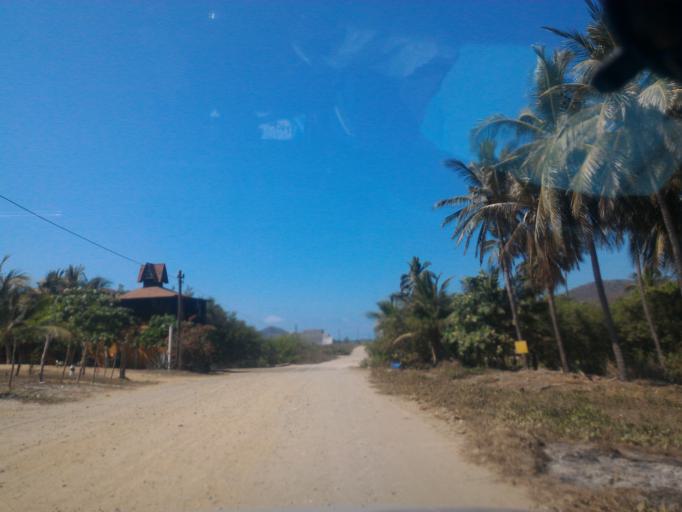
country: MX
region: Michoacan
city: Coahuayana Viejo
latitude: 18.5859
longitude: -103.6786
